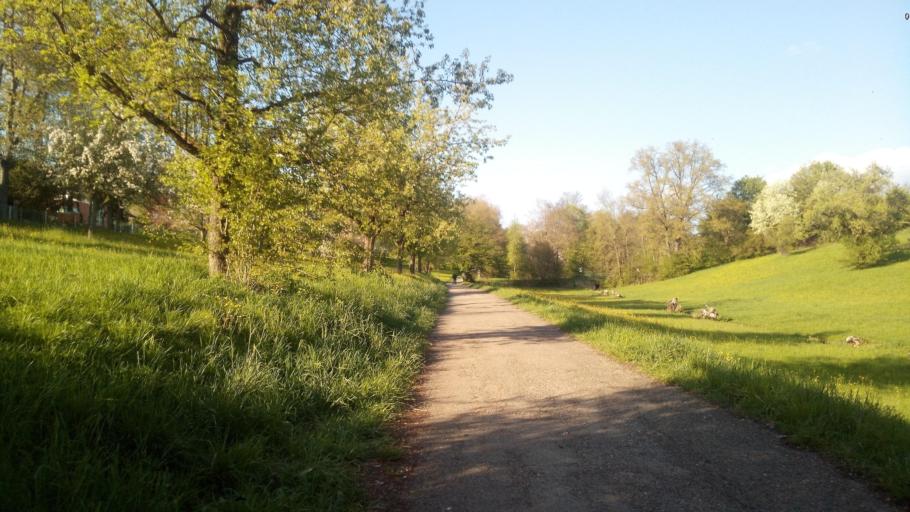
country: DE
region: Baden-Wuerttemberg
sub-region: Regierungsbezirk Stuttgart
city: Goeppingen
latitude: 48.7107
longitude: 9.6705
